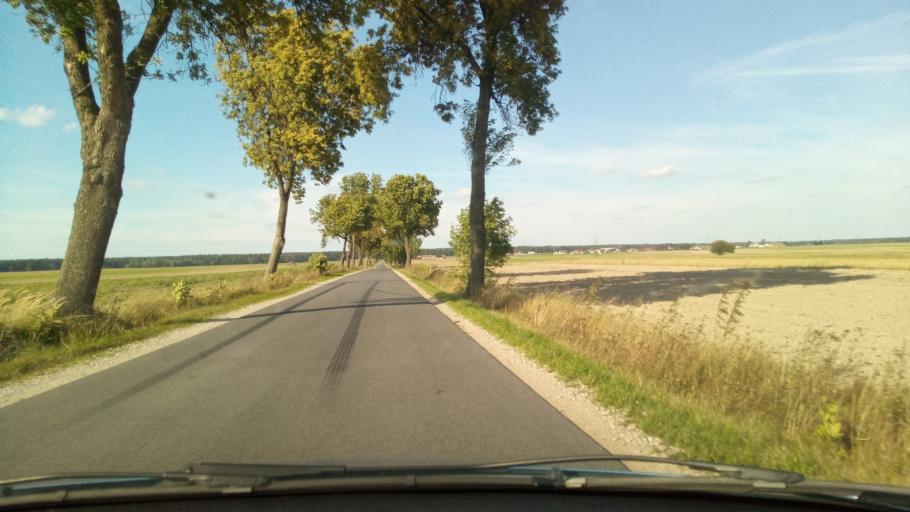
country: PL
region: Lodz Voivodeship
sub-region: Powiat piotrkowski
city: Sulejow
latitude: 51.3904
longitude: 19.8206
